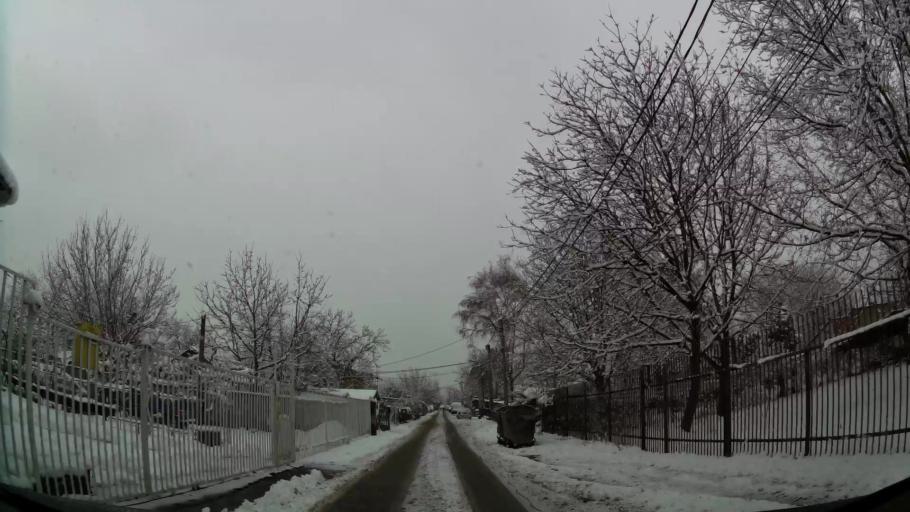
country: RS
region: Central Serbia
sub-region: Belgrade
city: Novi Beograd
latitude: 44.8072
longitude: 20.4393
